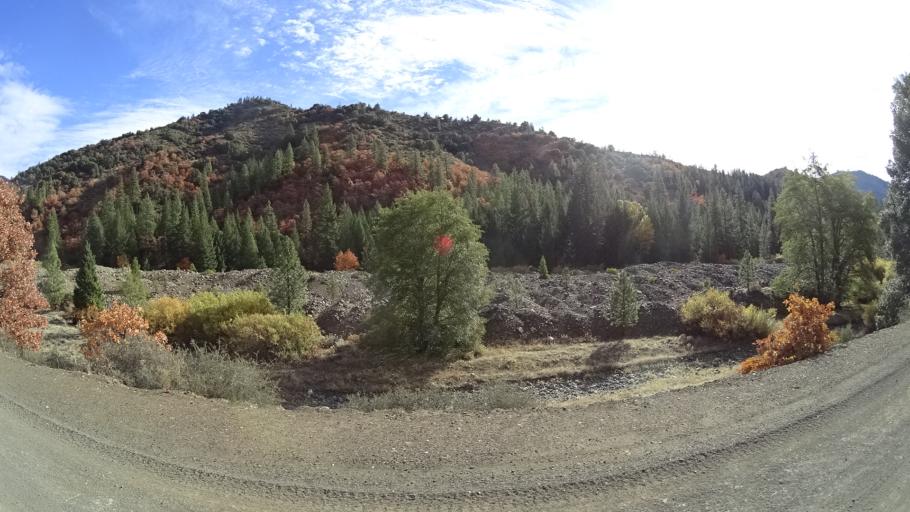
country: US
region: California
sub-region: Siskiyou County
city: Yreka
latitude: 41.7034
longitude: -122.8168
